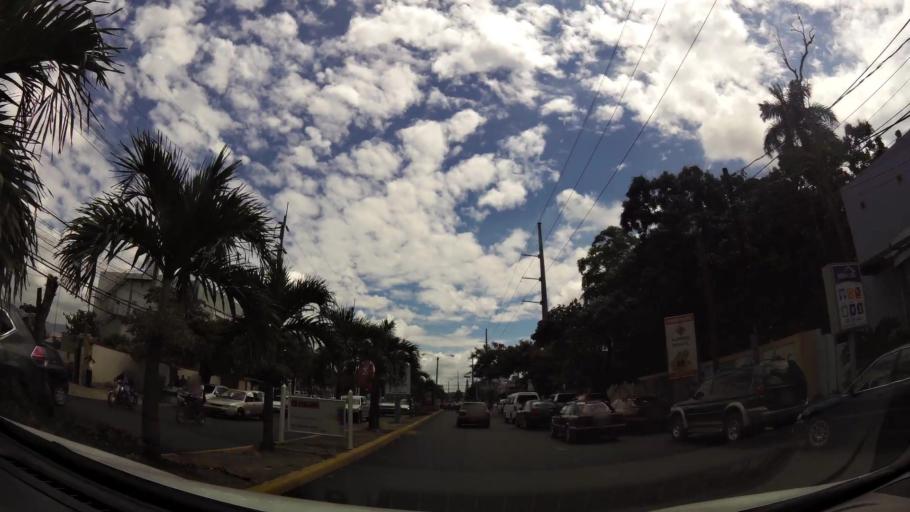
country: DO
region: Santiago
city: Santiago de los Caballeros
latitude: 19.4589
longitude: -70.6796
